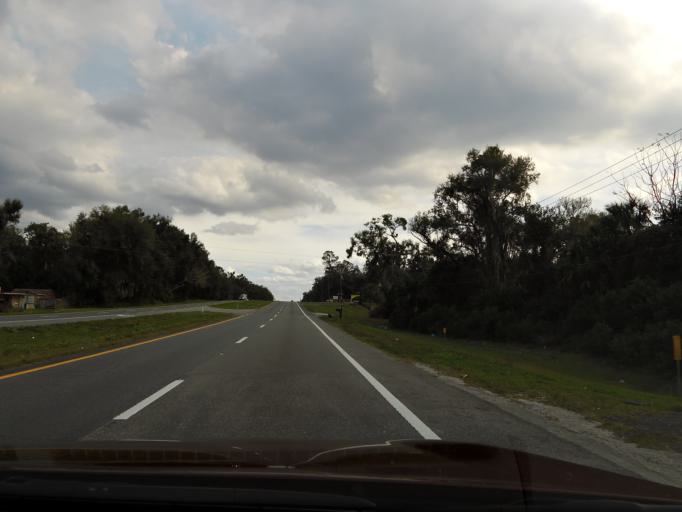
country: US
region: Florida
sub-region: Volusia County
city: De Leon Springs
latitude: 29.1109
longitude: -81.3486
